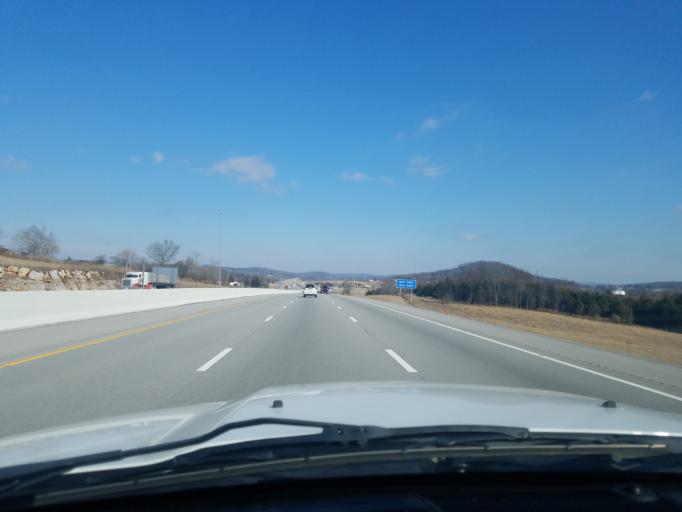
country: US
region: Kentucky
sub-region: Hart County
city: Horse Cave
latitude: 37.2293
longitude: -85.9309
